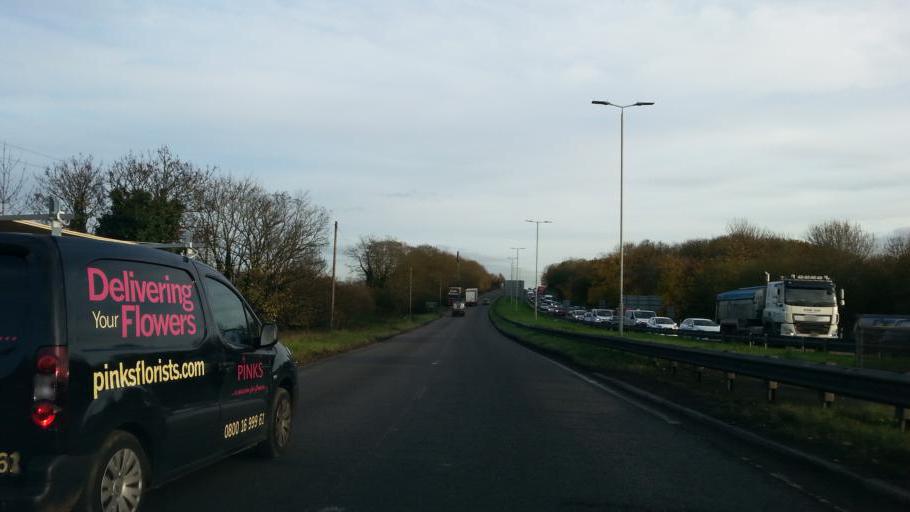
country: GB
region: England
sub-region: Hertfordshire
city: St Albans
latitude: 51.7327
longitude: -0.3436
